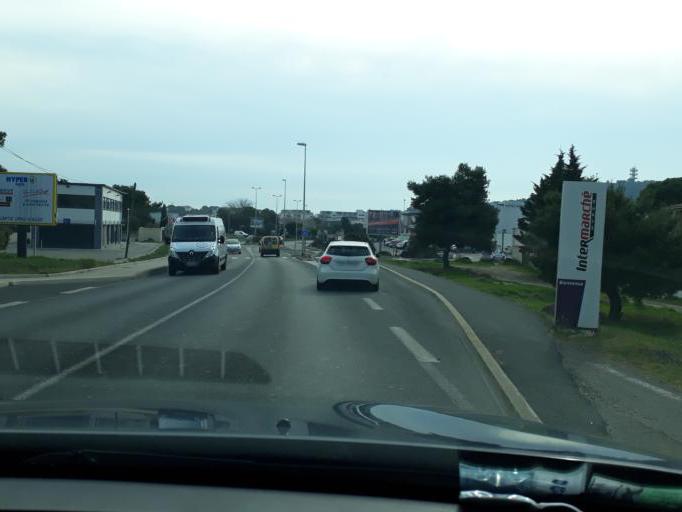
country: FR
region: Languedoc-Roussillon
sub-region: Departement de l'Herault
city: Agde
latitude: 43.3089
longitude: 3.4892
